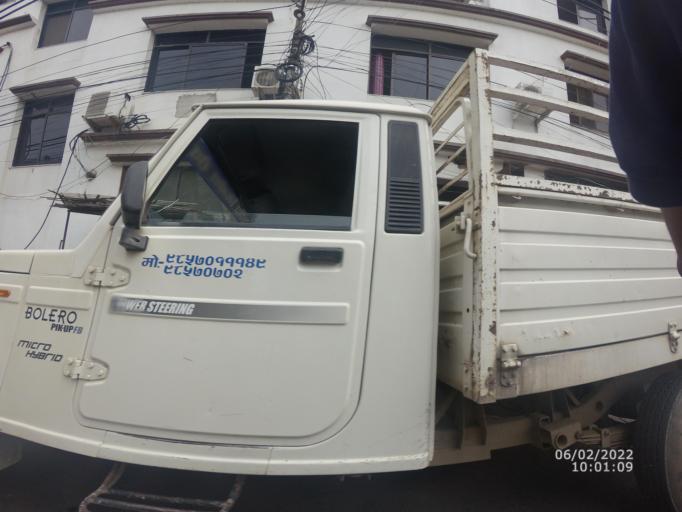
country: NP
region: Western Region
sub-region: Lumbini Zone
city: Bhairahawa
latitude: 27.5056
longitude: 83.4509
